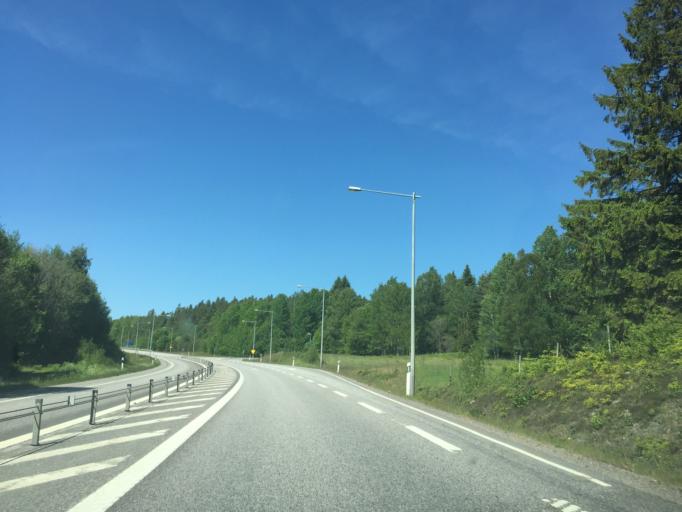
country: SE
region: OEstergoetland
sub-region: Motala Kommun
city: Motala
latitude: 58.6253
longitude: 14.9805
